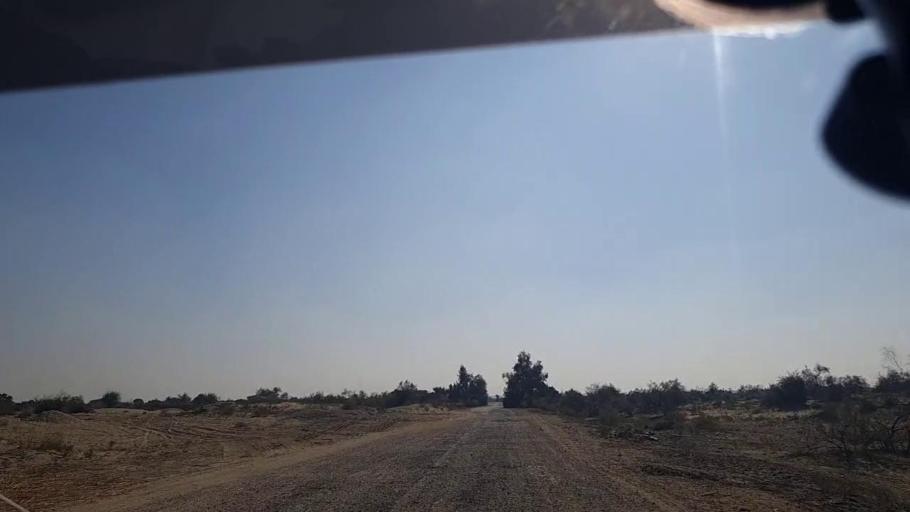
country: PK
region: Sindh
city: Khanpur
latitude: 27.5702
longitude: 69.3050
